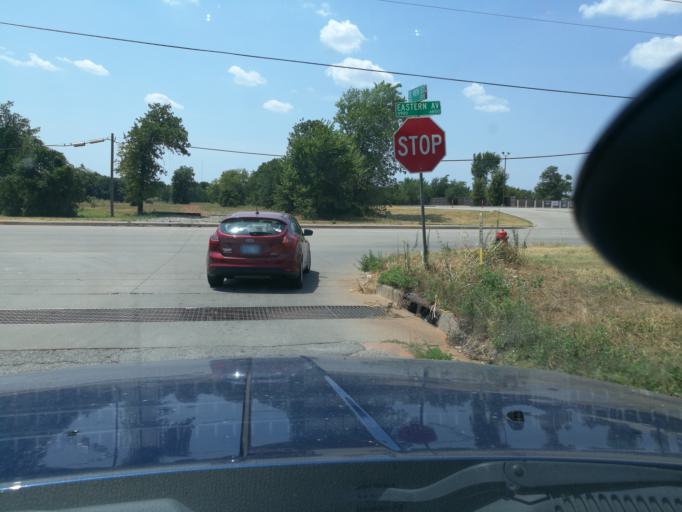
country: US
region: Oklahoma
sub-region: Oklahoma County
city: Del City
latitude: 35.4171
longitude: -97.4767
